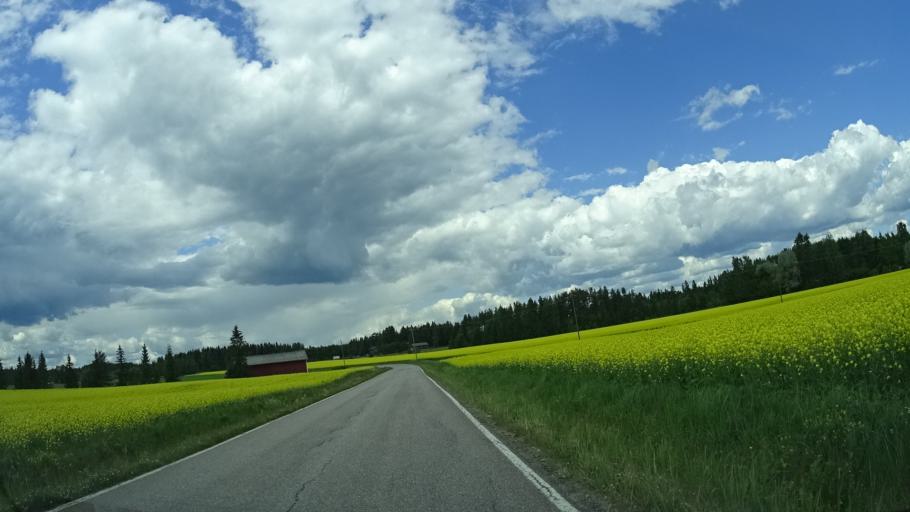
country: FI
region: Uusimaa
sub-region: Helsinki
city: Espoo
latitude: 60.4044
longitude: 24.6117
